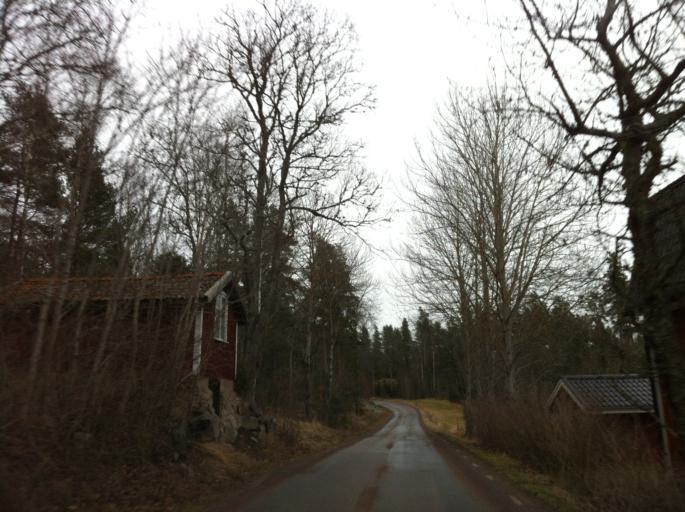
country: SE
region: Kalmar
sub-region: Vasterviks Kommun
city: Forserum
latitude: 57.9248
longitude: 16.5570
